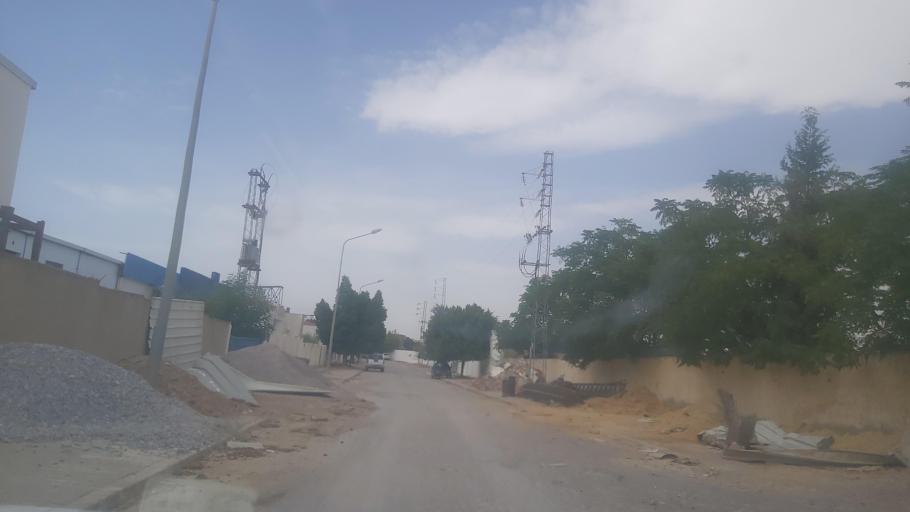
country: TN
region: Silyanah
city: Bu `Aradah
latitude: 36.3533
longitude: 9.6345
